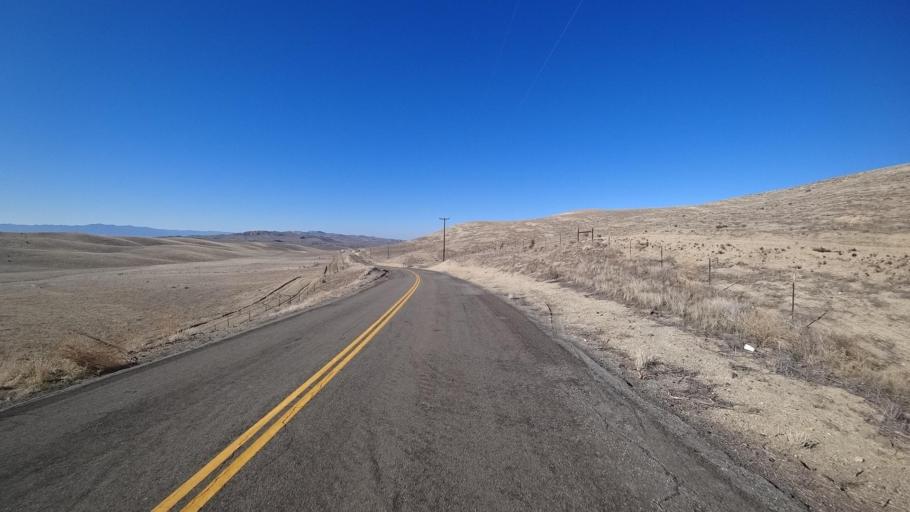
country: US
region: California
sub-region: Kern County
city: Maricopa
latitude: 34.9512
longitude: -119.4243
